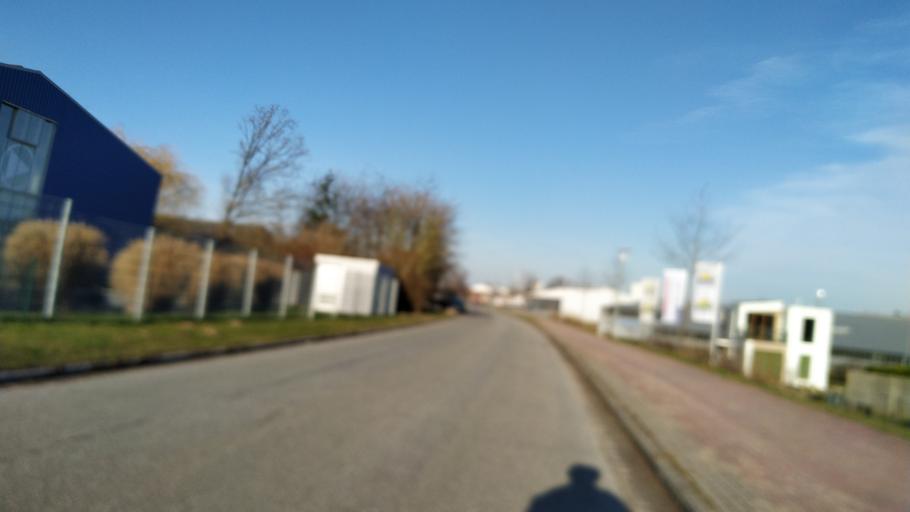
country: DE
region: Schleswig-Holstein
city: Neustadt in Holstein
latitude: 54.0933
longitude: 10.7950
